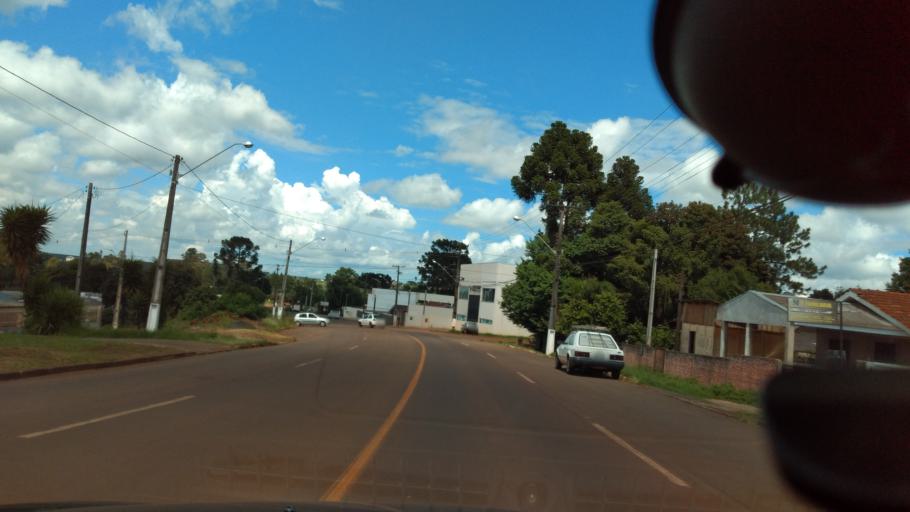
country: BR
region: Parana
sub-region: Guarapuava
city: Guarapuava
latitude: -25.3929
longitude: -51.4985
